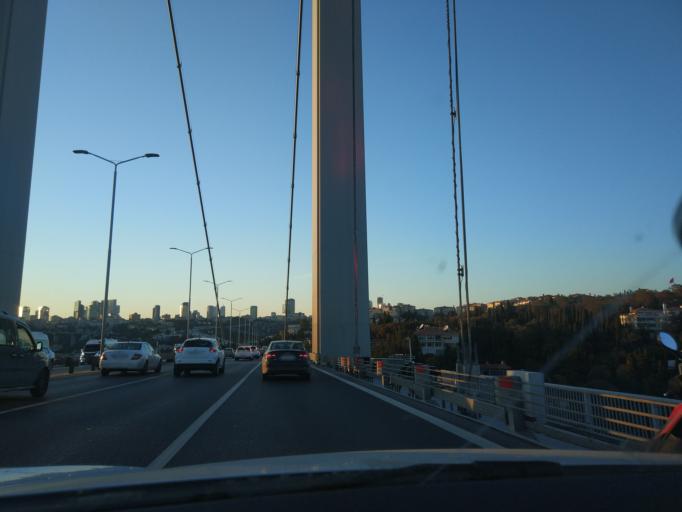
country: TR
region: Istanbul
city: UEskuedar
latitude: 41.0491
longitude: 29.0308
